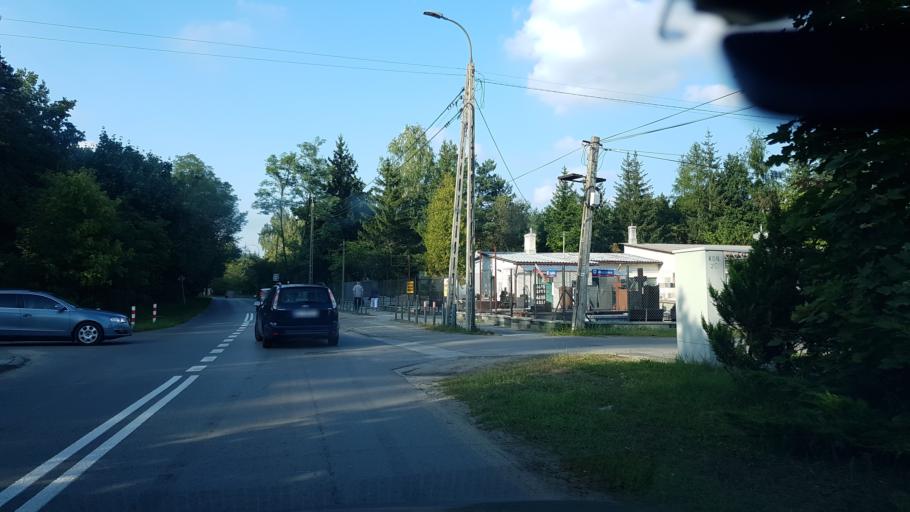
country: PL
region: Masovian Voivodeship
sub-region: Powiat piaseczynski
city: Konstancin-Jeziorna
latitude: 52.0678
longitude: 21.0998
